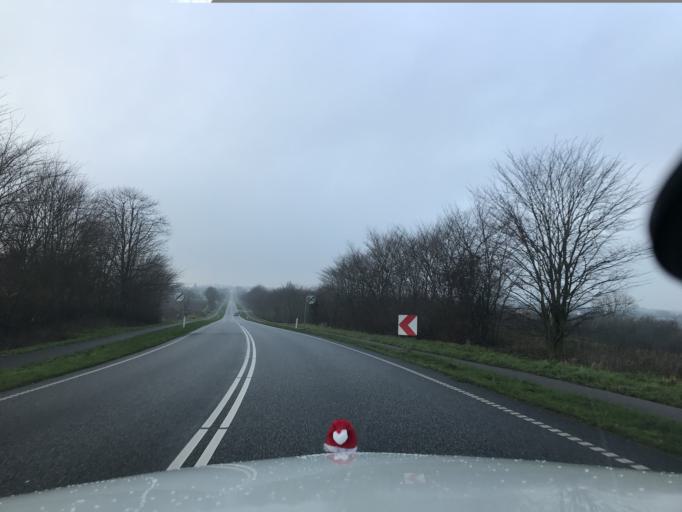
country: DK
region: South Denmark
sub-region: Sonderborg Kommune
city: Dybbol
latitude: 54.9082
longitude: 9.7446
